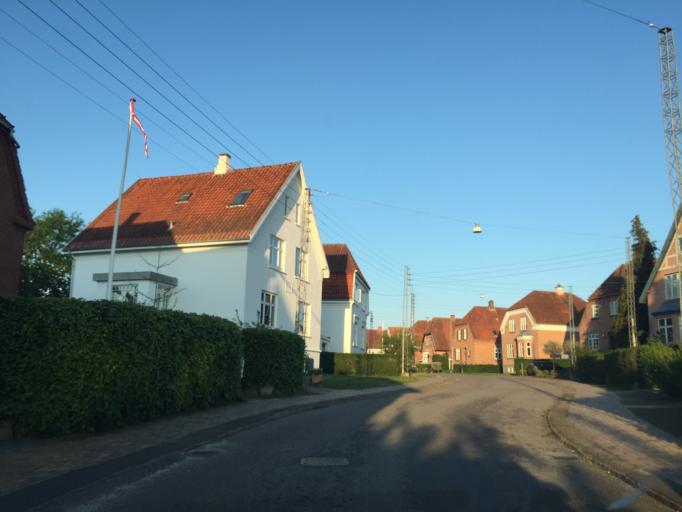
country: DK
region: South Denmark
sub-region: Odense Kommune
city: Odense
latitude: 55.3859
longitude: 10.3931
